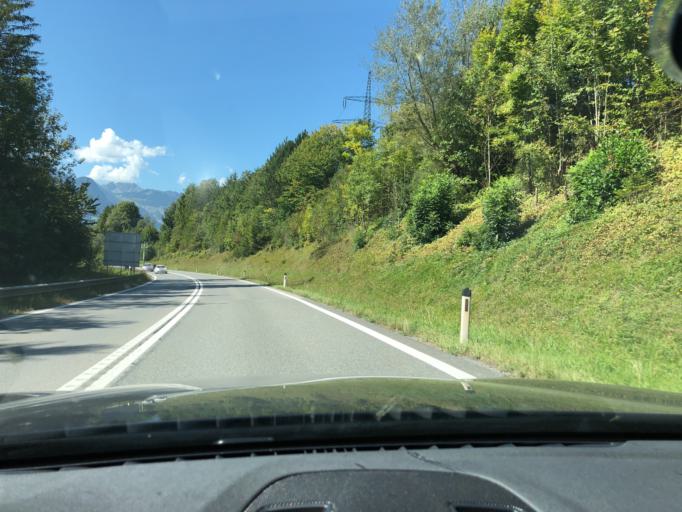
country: AT
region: Vorarlberg
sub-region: Politischer Bezirk Bludenz
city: Innerbraz
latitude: 47.1458
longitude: 9.8877
